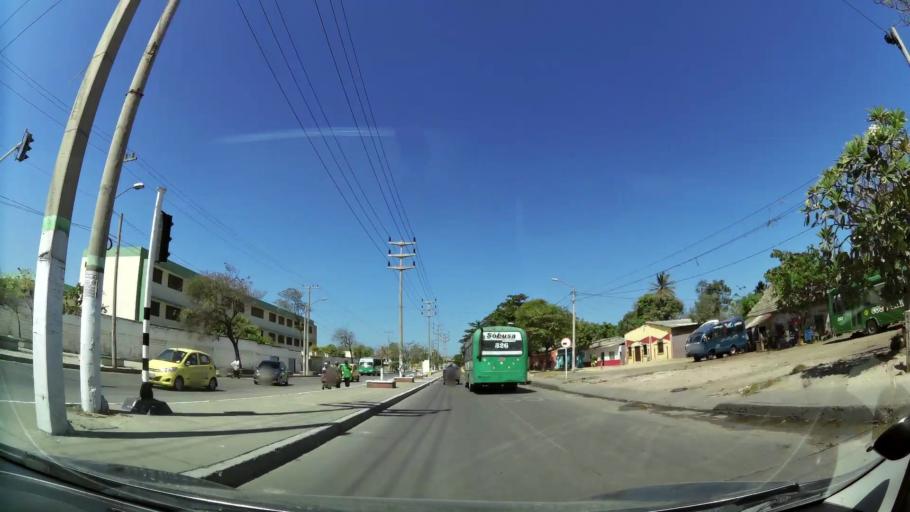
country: CO
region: Atlantico
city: Barranquilla
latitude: 10.9680
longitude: -74.7743
